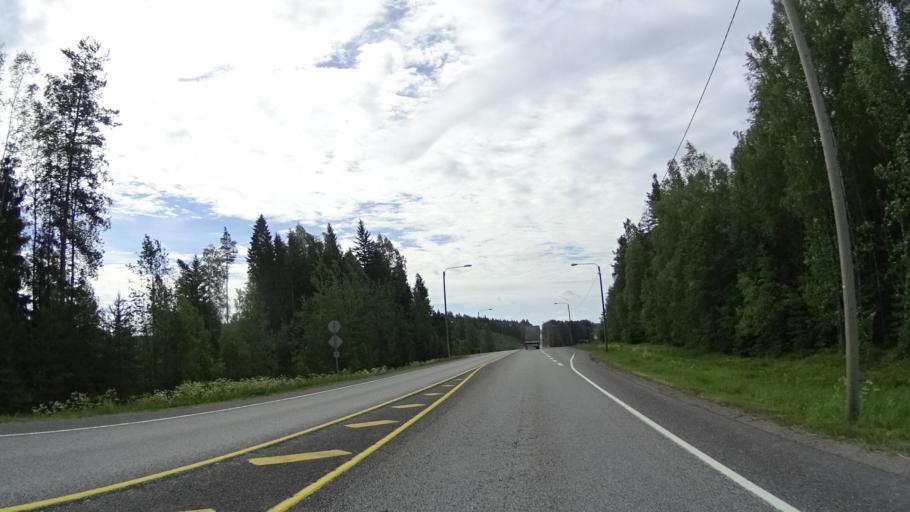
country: FI
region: Uusimaa
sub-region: Helsinki
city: Karkkila
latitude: 60.5089
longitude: 24.2630
